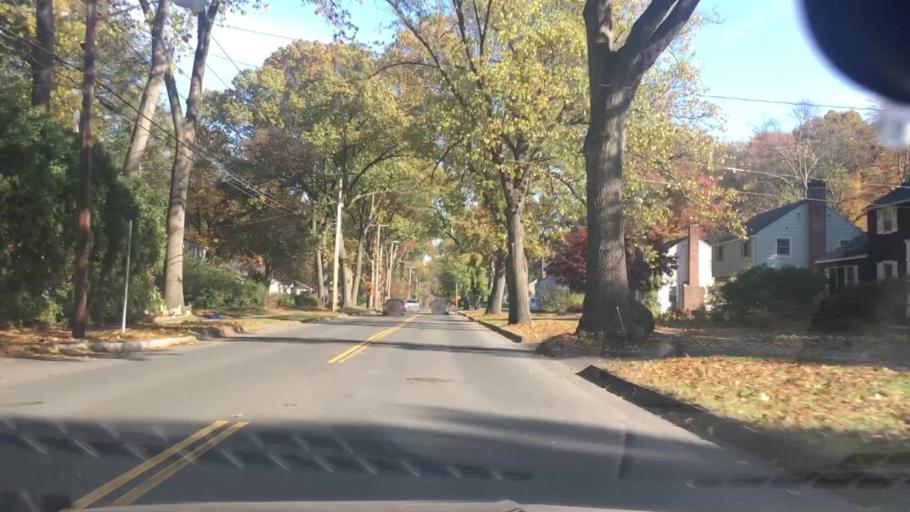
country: US
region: Connecticut
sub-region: Hartford County
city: Sherwood Manor
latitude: 42.0319
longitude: -72.5713
